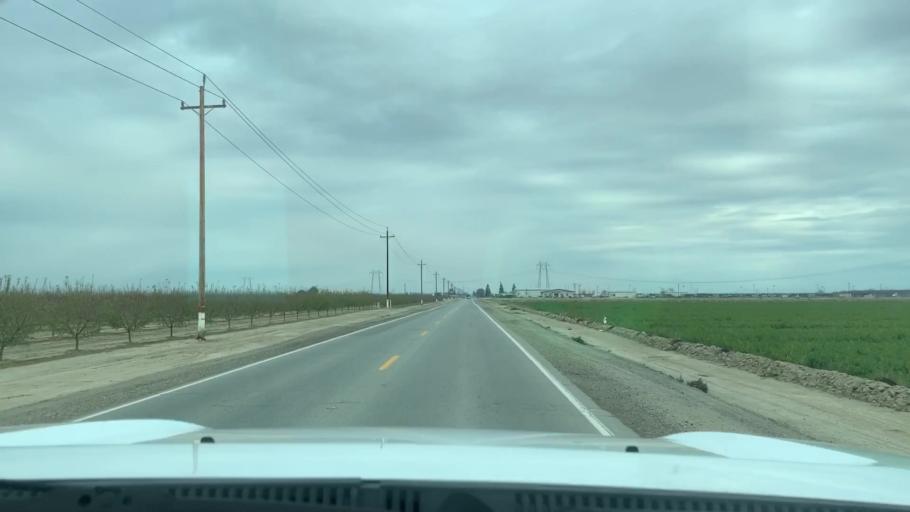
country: US
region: California
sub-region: Kern County
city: Rosedale
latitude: 35.3569
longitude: -119.2521
